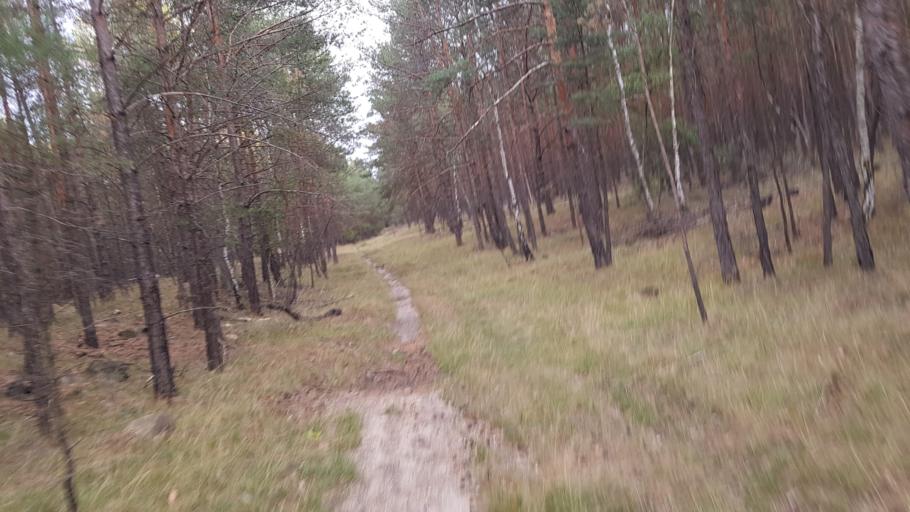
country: DE
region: Brandenburg
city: Trobitz
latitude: 51.5840
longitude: 13.4368
